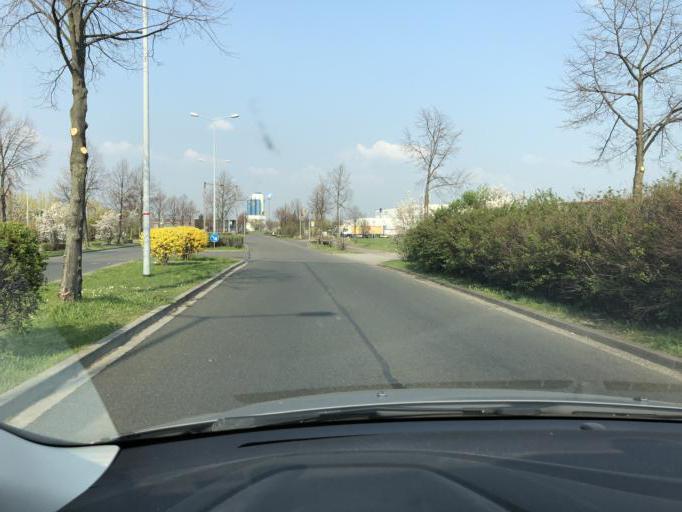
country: DE
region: Saxony
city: Zwochau
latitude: 51.4172
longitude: 12.3060
